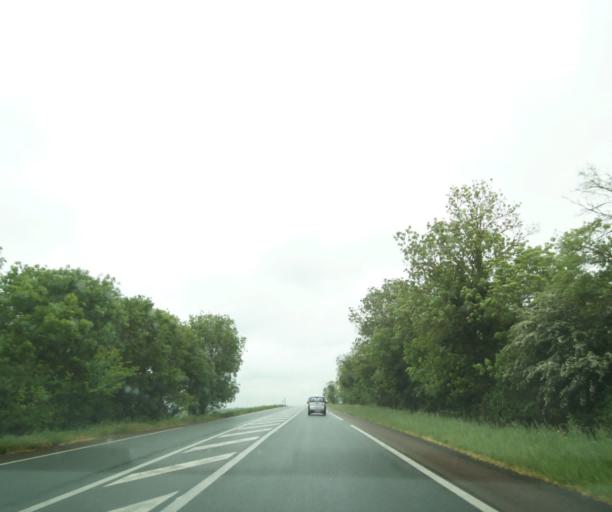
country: FR
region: Poitou-Charentes
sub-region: Departement de la Charente-Maritime
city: Les Gonds
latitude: 45.6730
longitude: -0.6022
